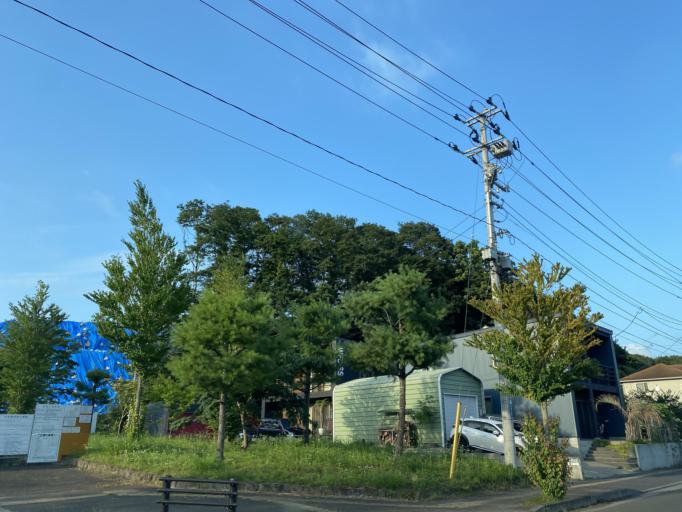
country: JP
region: Miyagi
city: Tomiya
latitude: 38.3895
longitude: 140.8699
